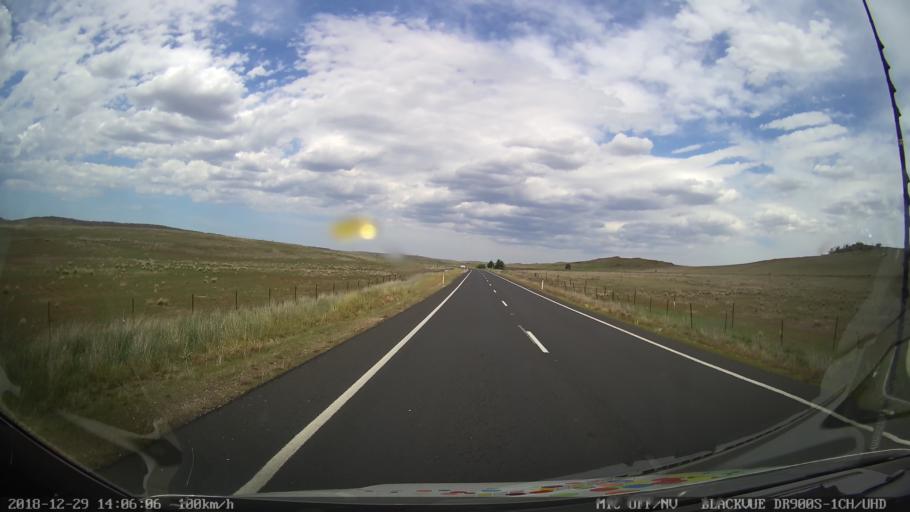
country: AU
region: New South Wales
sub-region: Cooma-Monaro
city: Cooma
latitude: -36.3395
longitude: 149.1974
